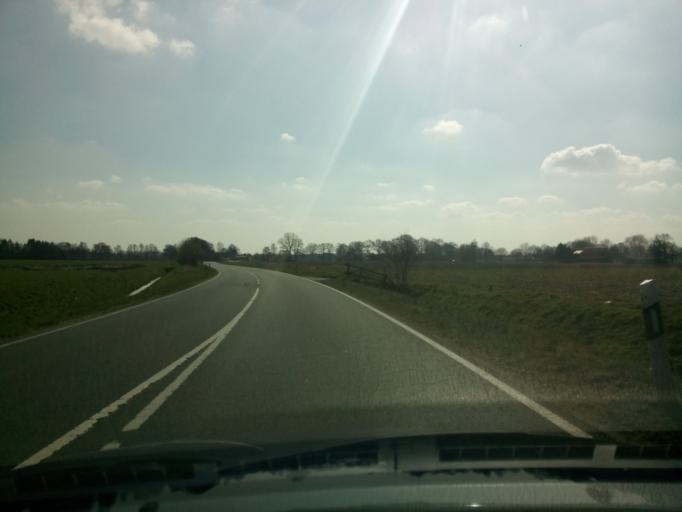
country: DE
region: Lower Saxony
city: Golenkamp
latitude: 52.5011
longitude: 6.9487
